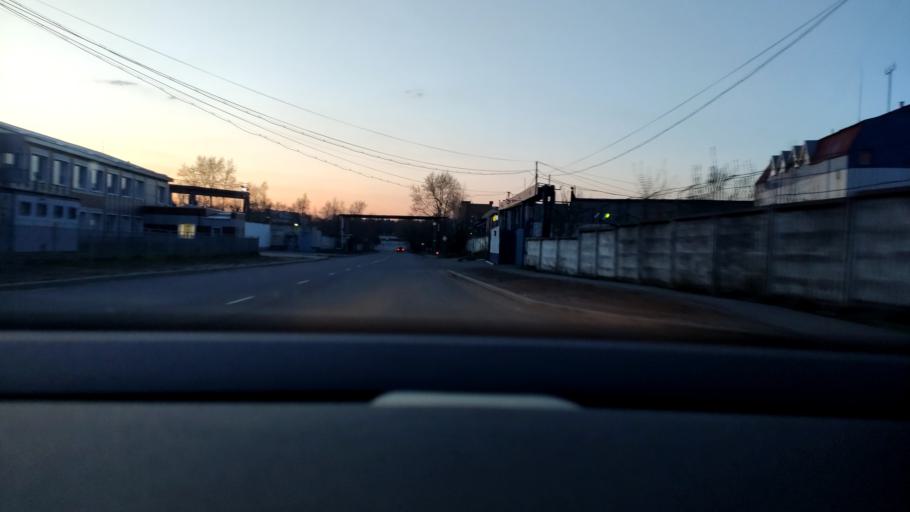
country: RU
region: Moskovskaya
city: Reutov
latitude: 55.7697
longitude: 37.8794
